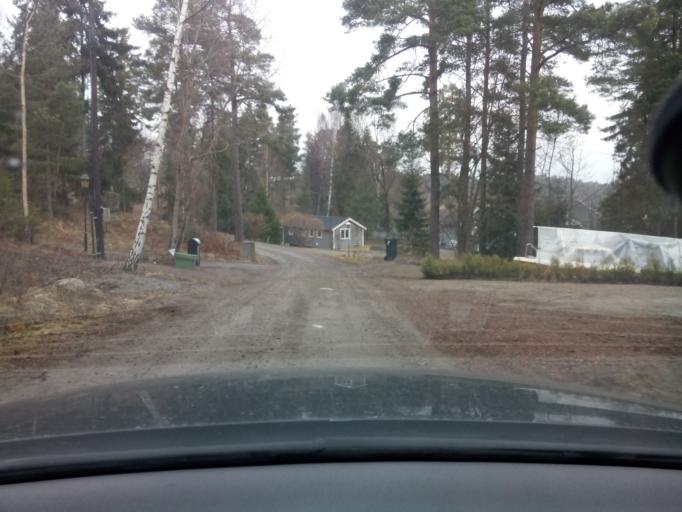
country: SE
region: Soedermanland
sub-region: Trosa Kommun
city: Trosa
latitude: 58.8904
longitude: 17.5790
